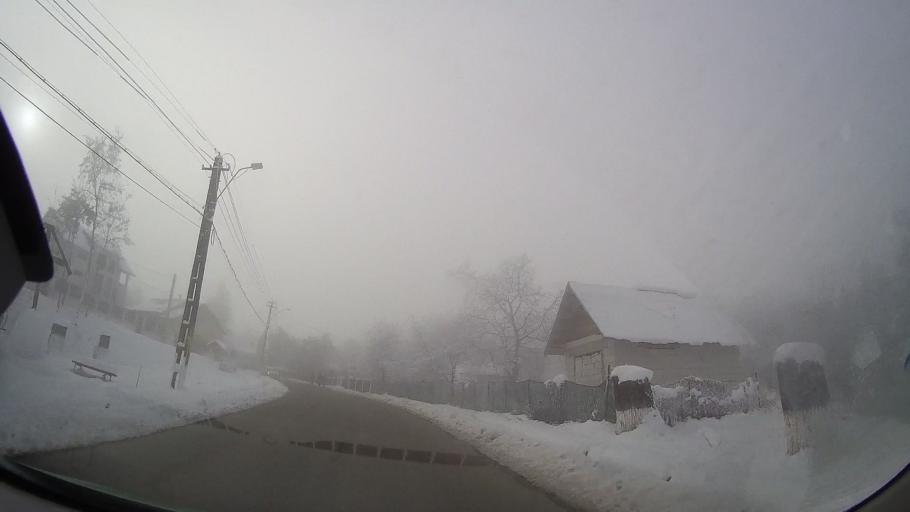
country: RO
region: Iasi
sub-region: Comuna Valea Seaca
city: Topile
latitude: 47.2605
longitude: 26.6673
